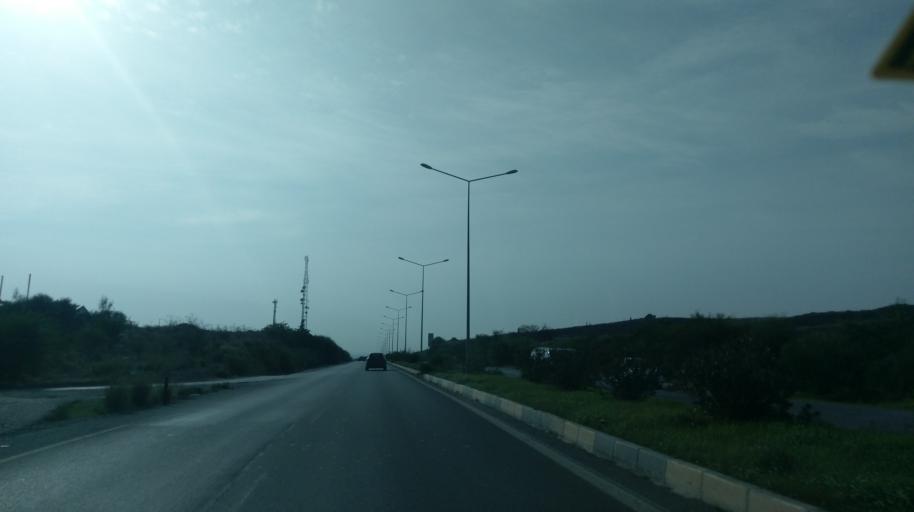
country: CY
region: Lefkosia
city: Nicosia
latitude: 35.2349
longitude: 33.3117
